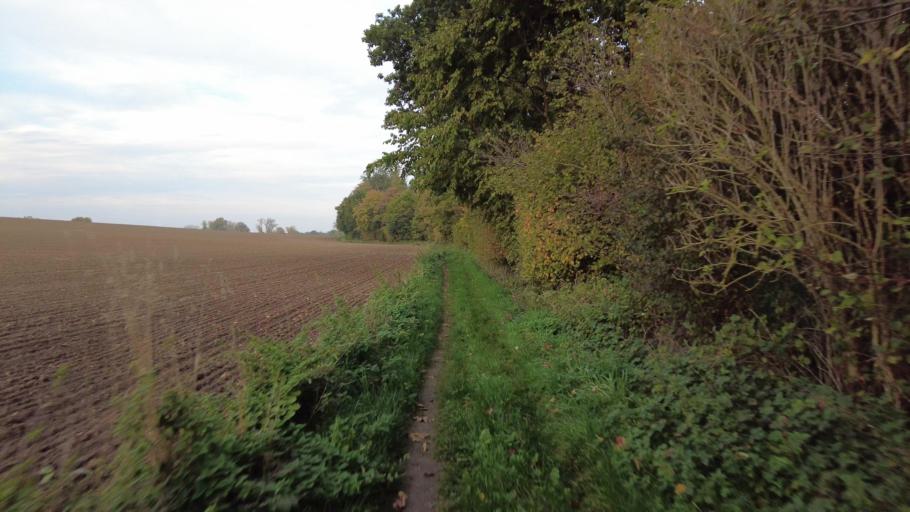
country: BE
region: Wallonia
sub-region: Province du Brabant Wallon
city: Jodoigne
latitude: 50.7319
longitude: 4.8739
